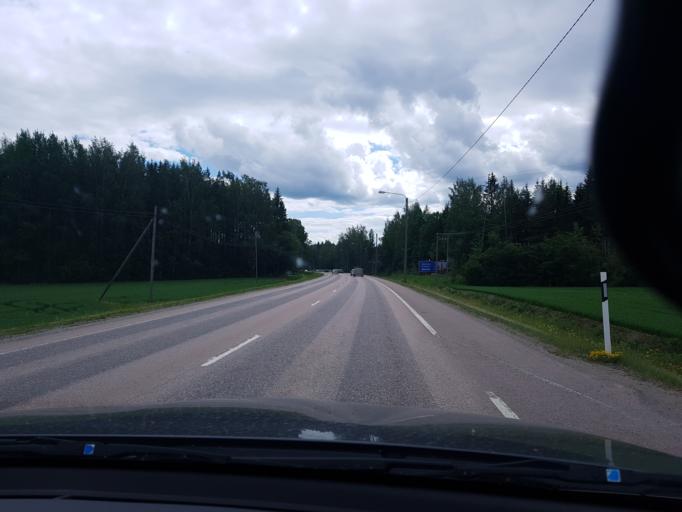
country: FI
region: Pirkanmaa
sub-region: Tampere
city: Paelkaene
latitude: 61.3592
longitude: 24.2450
